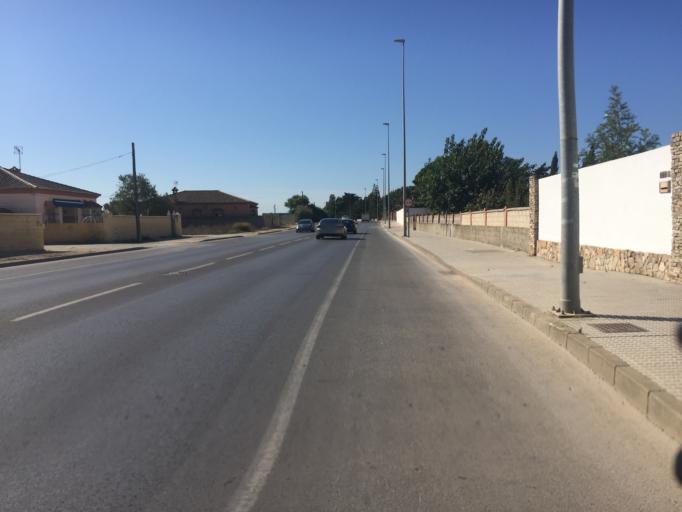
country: ES
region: Andalusia
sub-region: Provincia de Cadiz
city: Chiclana de la Frontera
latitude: 36.4055
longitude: -6.1664
